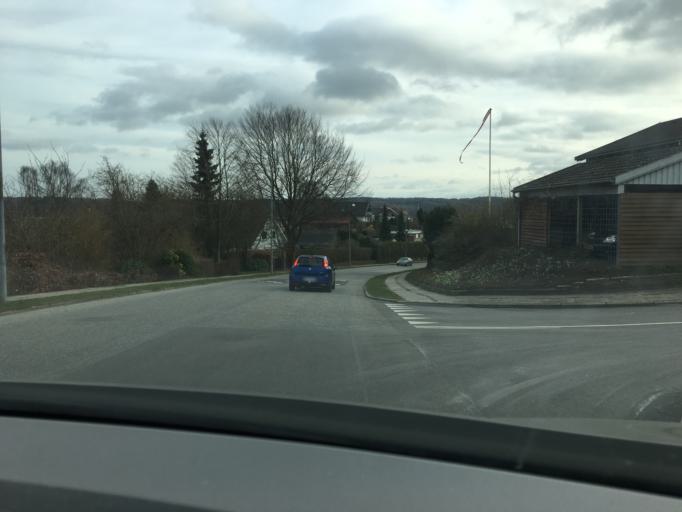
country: DK
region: South Denmark
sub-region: Vejle Kommune
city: Vejle
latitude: 55.7110
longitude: 9.5936
